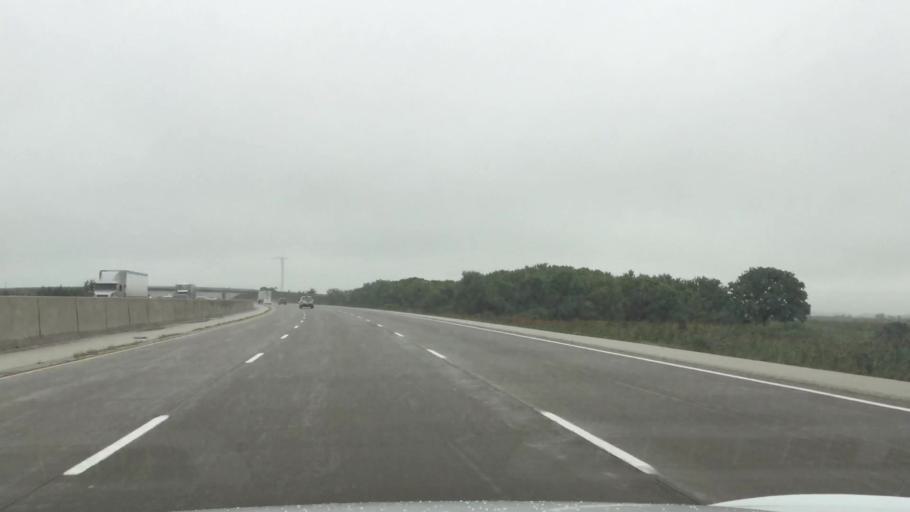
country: US
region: Michigan
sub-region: Wayne County
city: Grosse Pointe Farms
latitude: 42.2325
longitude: -82.6027
